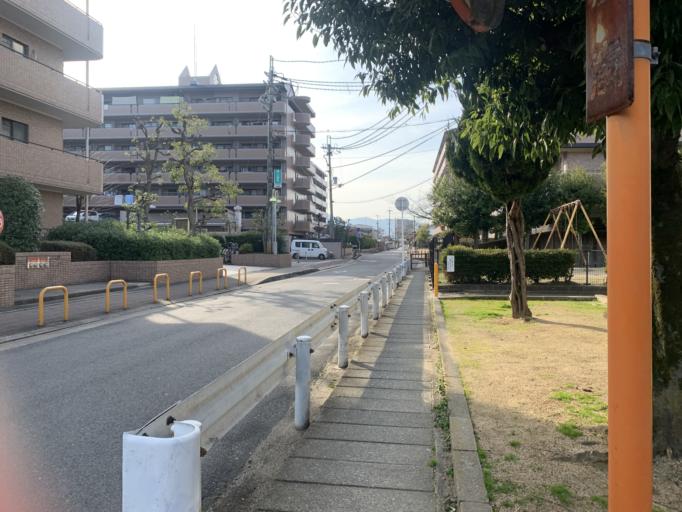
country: JP
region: Nara
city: Kashihara-shi
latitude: 34.5128
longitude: 135.7521
